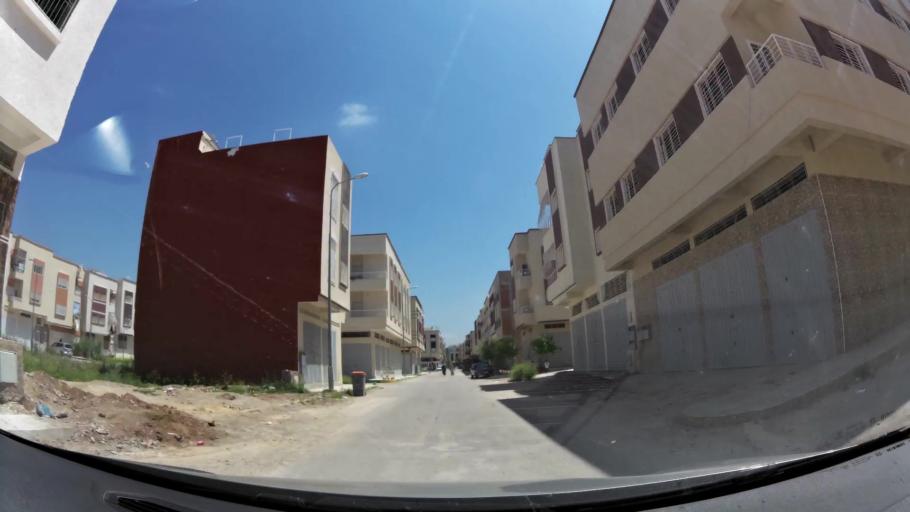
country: MA
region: Fes-Boulemane
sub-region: Fes
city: Fes
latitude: 34.0209
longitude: -5.0516
